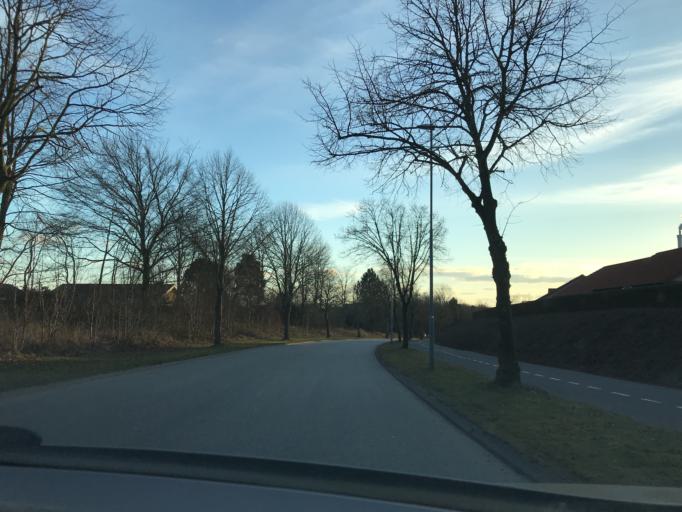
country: DK
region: South Denmark
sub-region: Middelfart Kommune
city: Norre Aby
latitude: 55.4583
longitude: 9.8839
